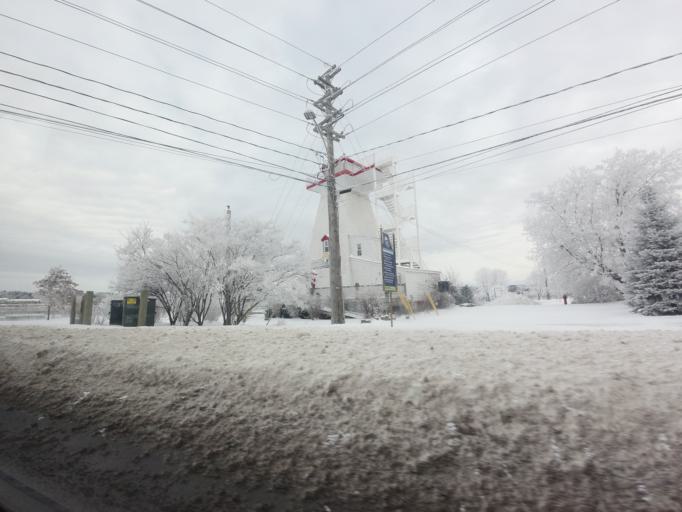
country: CA
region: New Brunswick
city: Fredericton
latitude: 45.9619
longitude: -66.6379
